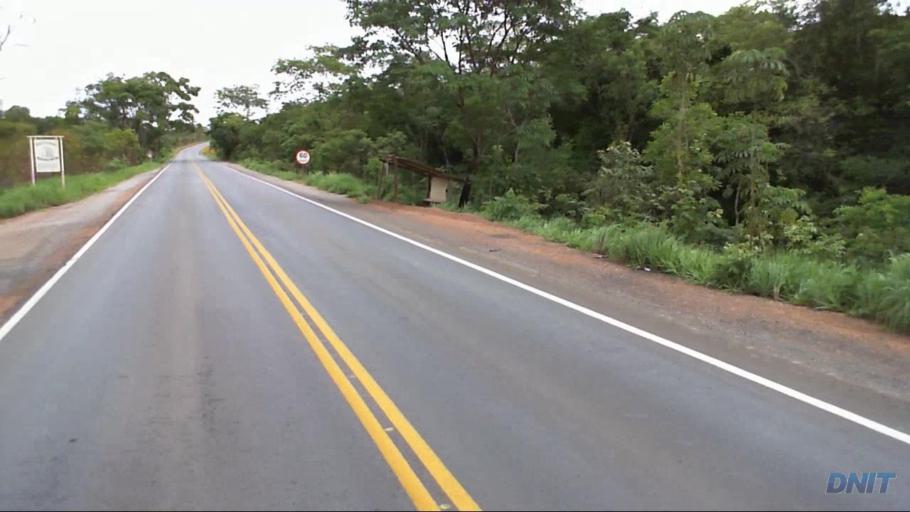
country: BR
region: Goias
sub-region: Padre Bernardo
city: Padre Bernardo
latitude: -15.4215
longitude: -48.1979
